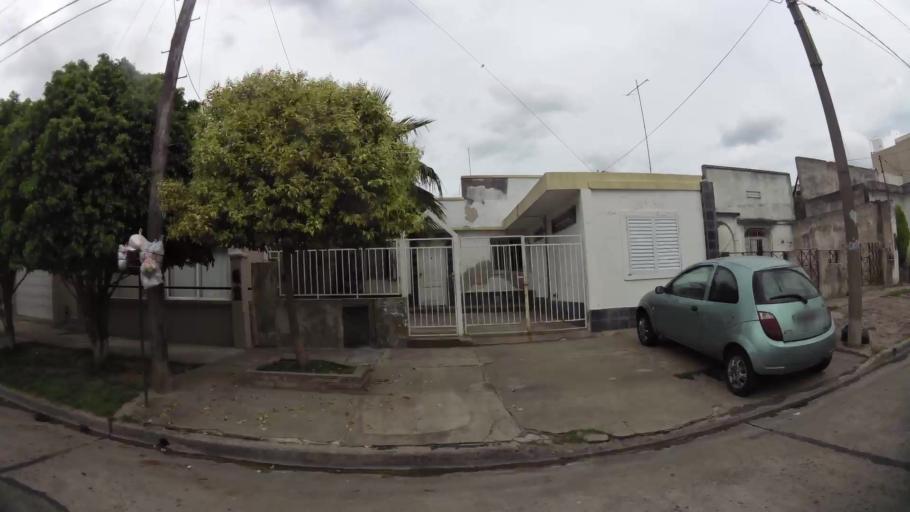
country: AR
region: Buenos Aires
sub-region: Partido de Campana
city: Campana
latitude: -34.1680
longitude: -58.9517
